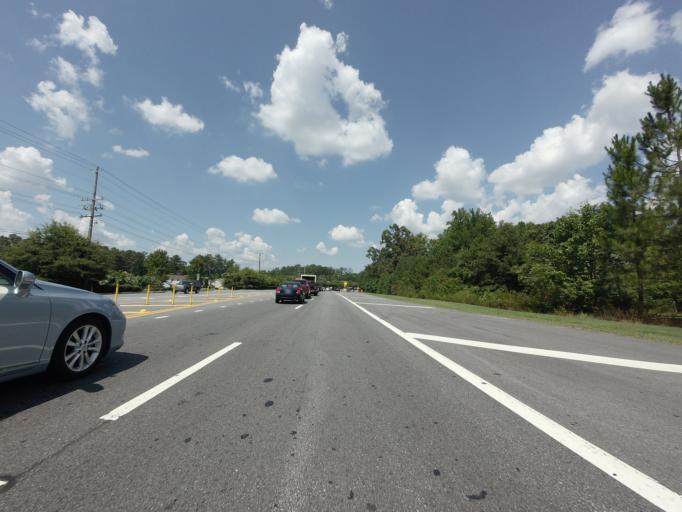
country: US
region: Georgia
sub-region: Fulton County
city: Johns Creek
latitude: 34.0592
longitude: -84.2277
